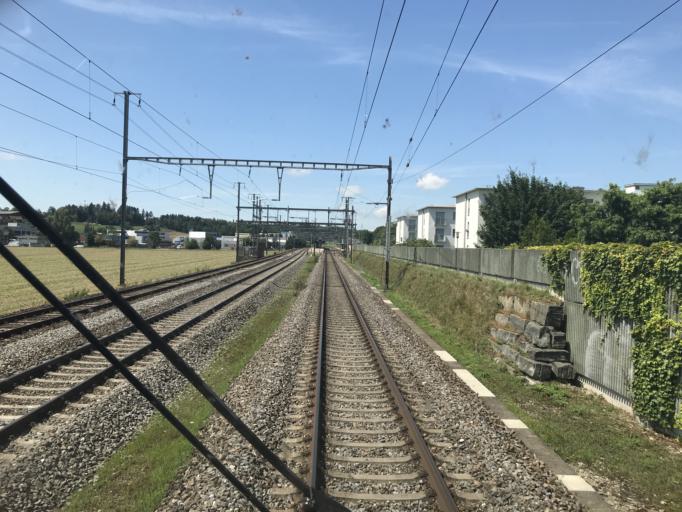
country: CH
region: Zurich
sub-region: Bezirk Buelach
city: Bassersdorf
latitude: 47.4378
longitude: 8.6308
